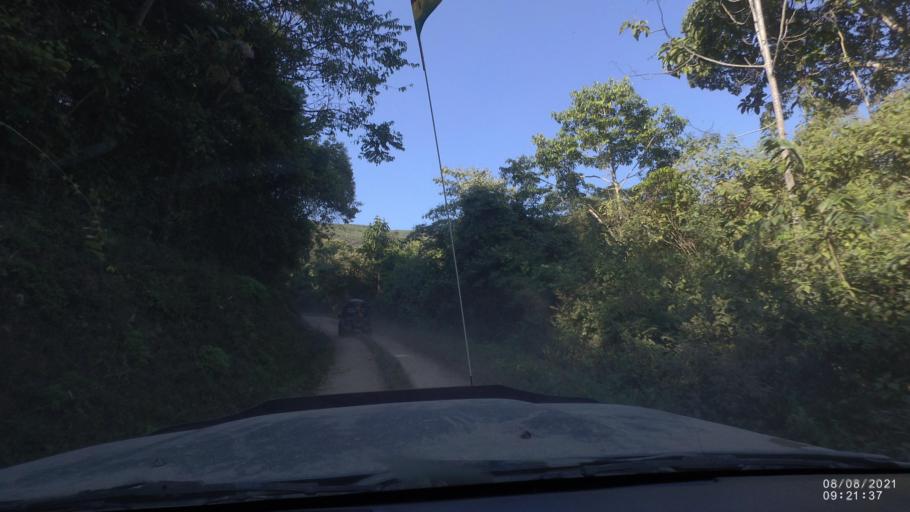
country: BO
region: La Paz
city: Quime
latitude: -16.5731
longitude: -66.7163
